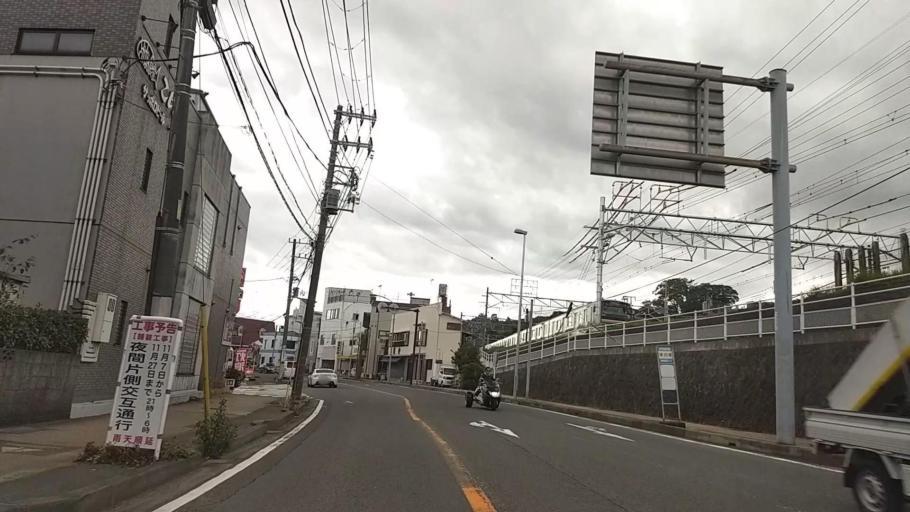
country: JP
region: Kanagawa
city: Odawara
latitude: 35.2404
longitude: 139.1460
